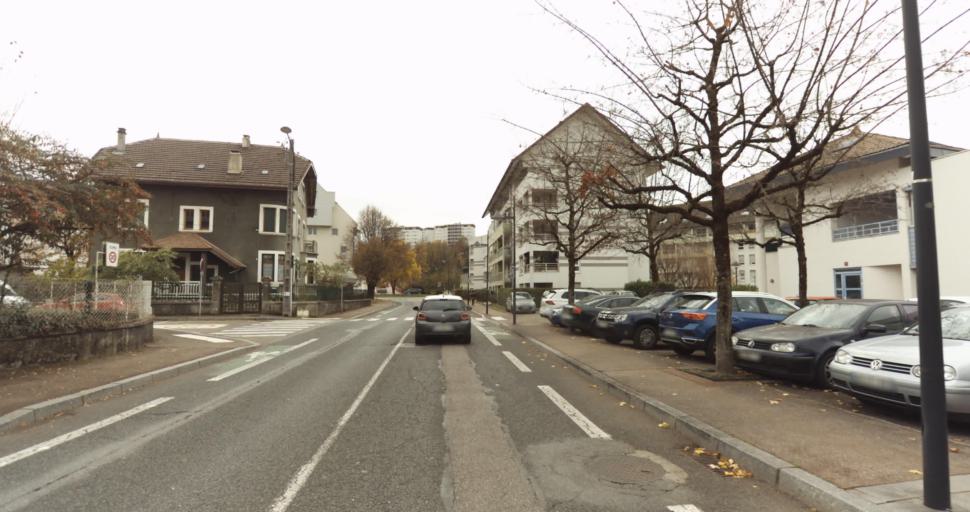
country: FR
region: Rhone-Alpes
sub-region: Departement de la Haute-Savoie
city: Annecy
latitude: 45.9057
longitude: 6.1086
